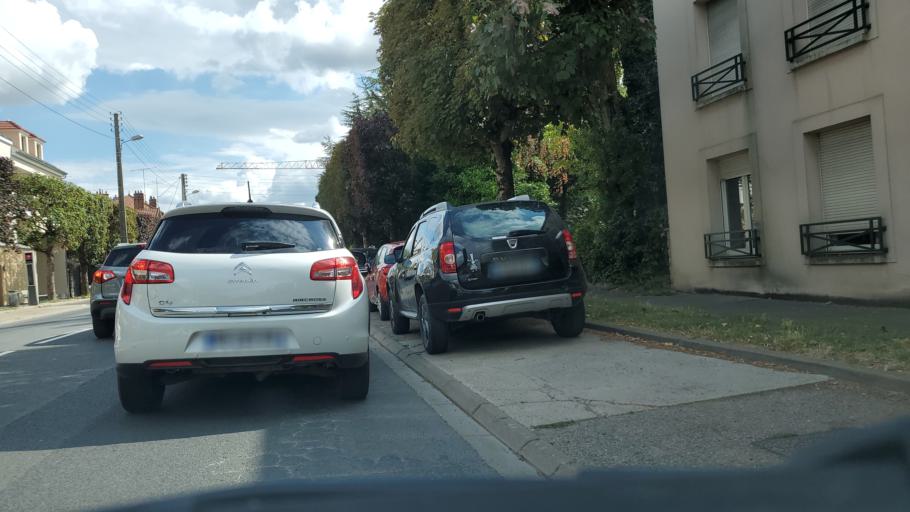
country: FR
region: Ile-de-France
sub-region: Departement de Seine-et-Marne
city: Coulommiers
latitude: 48.8053
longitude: 3.0845
